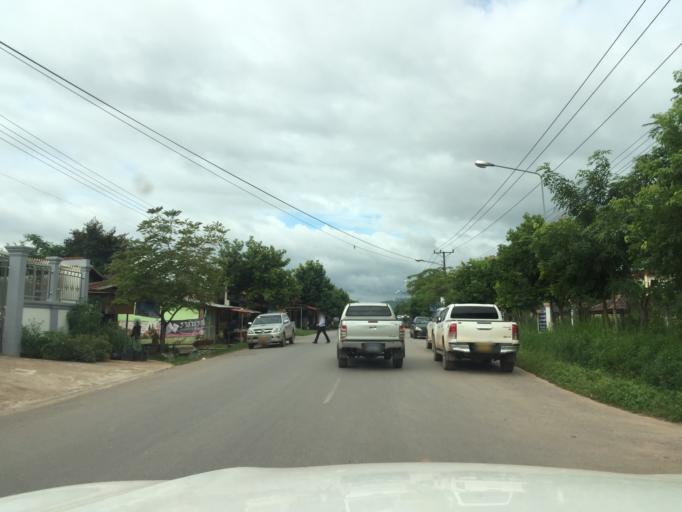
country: LA
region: Oudomxai
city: Muang Xay
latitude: 20.7004
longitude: 101.9926
